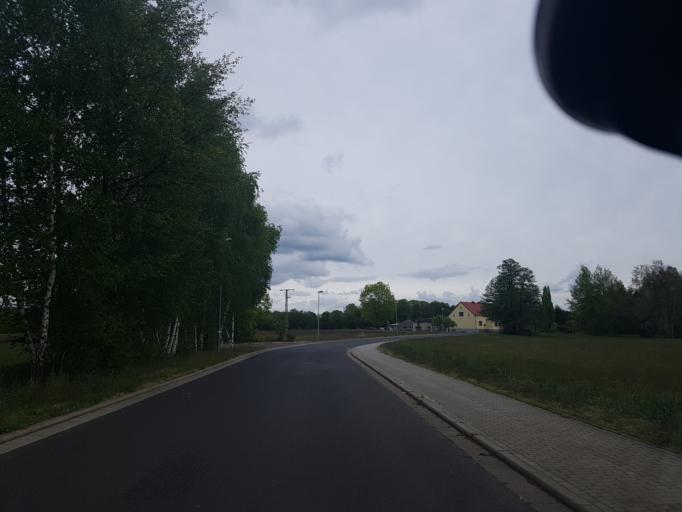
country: DE
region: Brandenburg
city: Tschernitz
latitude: 51.6223
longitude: 14.5977
